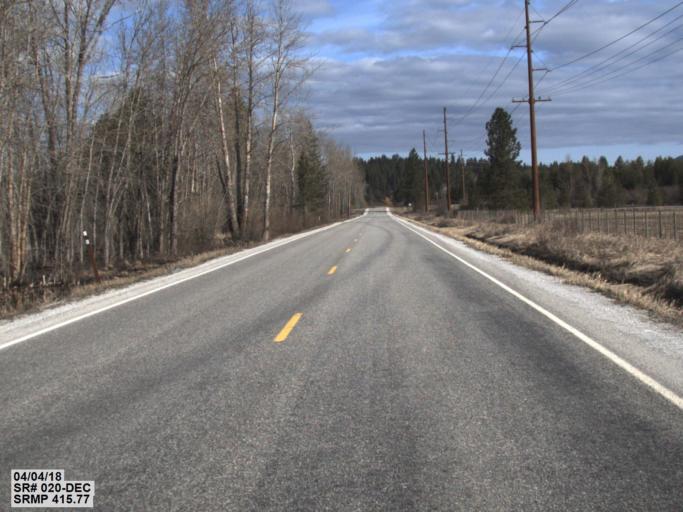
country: US
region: Washington
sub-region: Pend Oreille County
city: Newport
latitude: 48.3839
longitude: -117.3100
